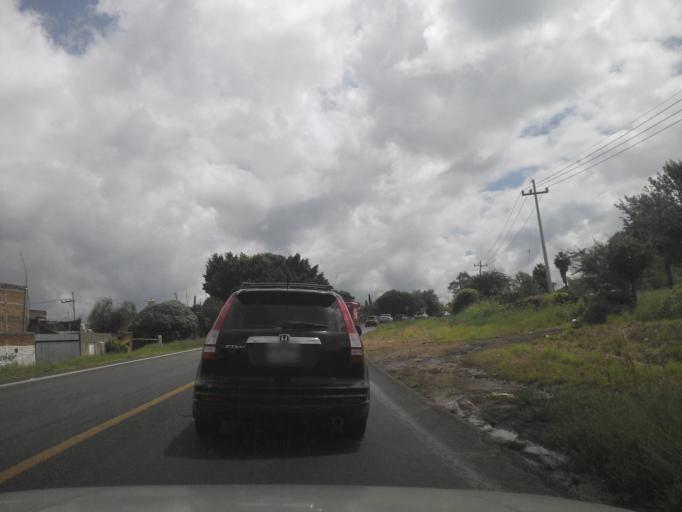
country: MX
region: Jalisco
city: Zapotlanejo
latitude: 20.6228
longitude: -103.0239
